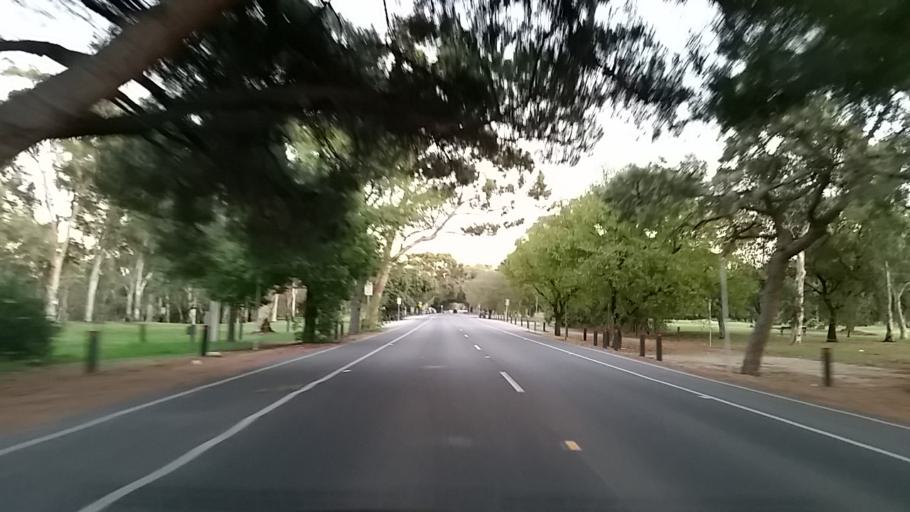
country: AU
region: South Australia
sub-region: Adelaide
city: North Adelaide
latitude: -34.9155
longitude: 138.5873
